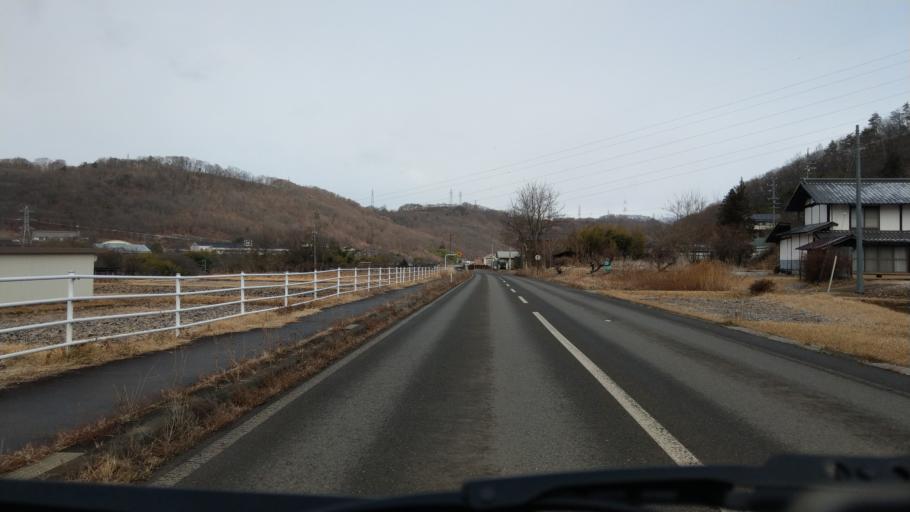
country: JP
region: Nagano
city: Kamimaruko
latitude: 36.3197
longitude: 138.3454
